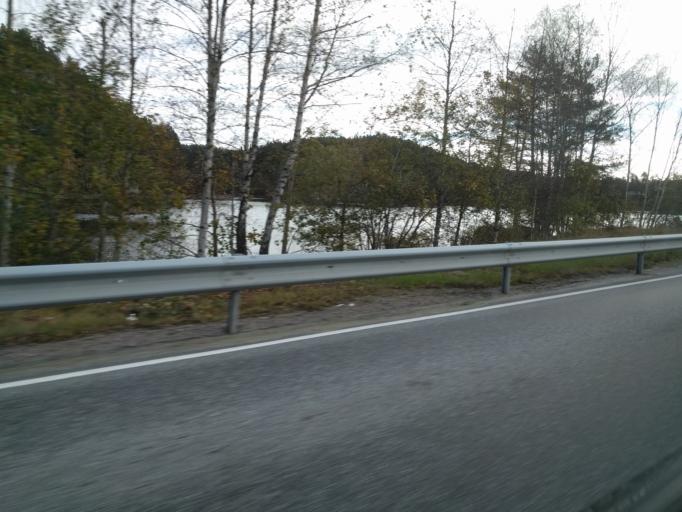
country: NO
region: Vest-Agder
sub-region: Kristiansand
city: Strai
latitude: 58.2506
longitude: 7.8642
